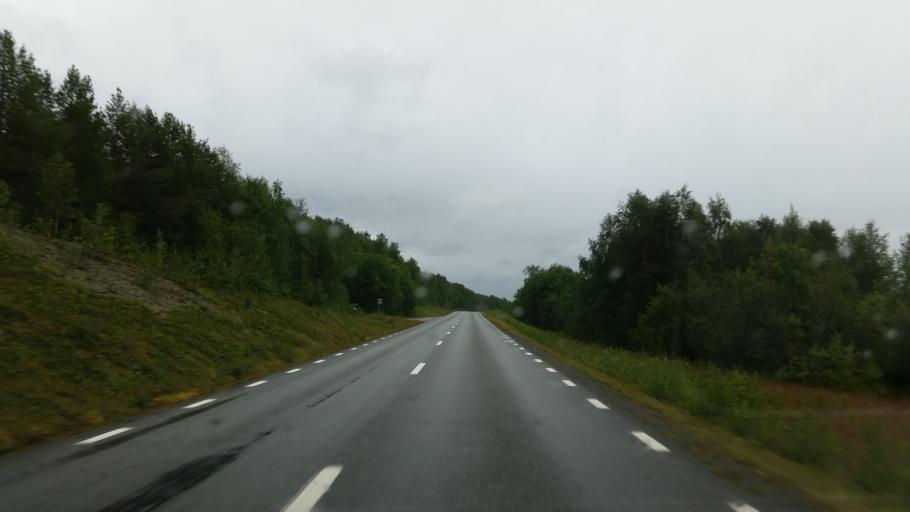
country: NO
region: Nordland
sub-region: Rana
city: Mo i Rana
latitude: 65.8598
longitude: 15.0258
